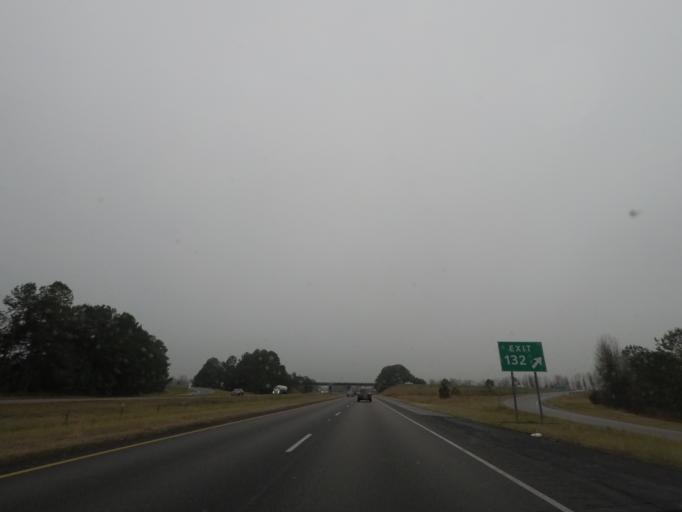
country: US
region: South Carolina
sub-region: Clarendon County
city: Manning
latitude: 33.8627
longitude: -80.1117
